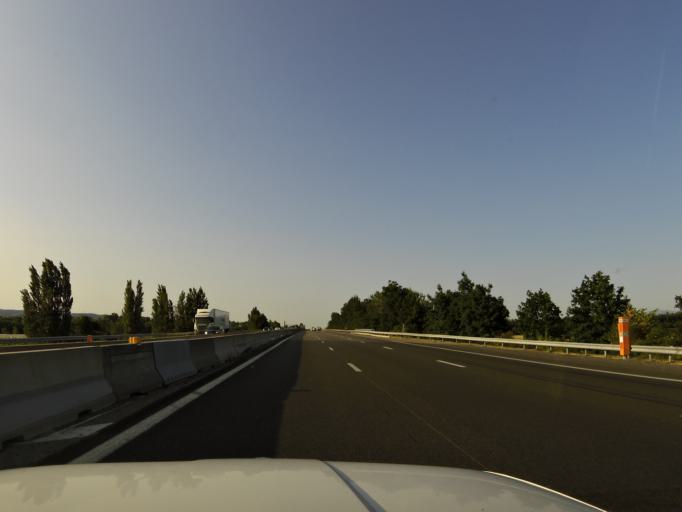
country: FR
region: Rhone-Alpes
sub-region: Departement de la Drome
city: Loriol-sur-Drome
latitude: 44.7630
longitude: 4.7971
